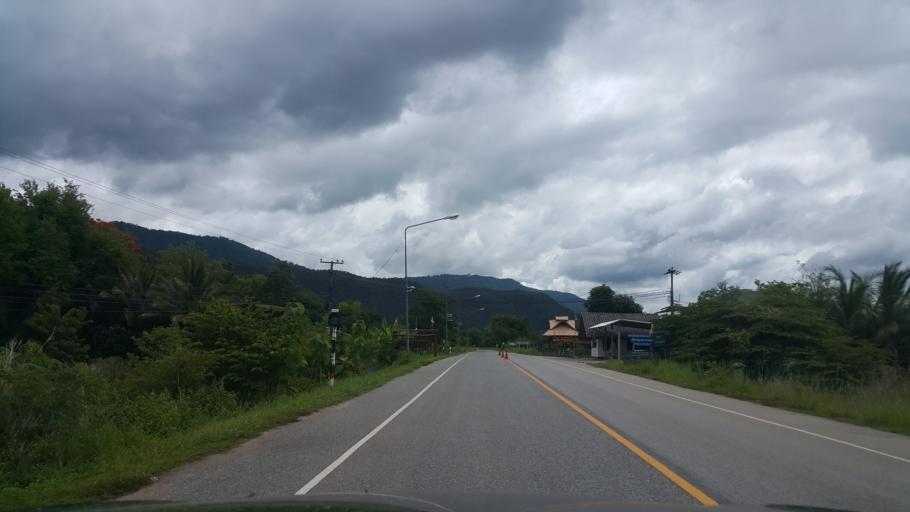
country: TH
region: Phitsanulok
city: Chat Trakan
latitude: 17.3038
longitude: 100.6674
